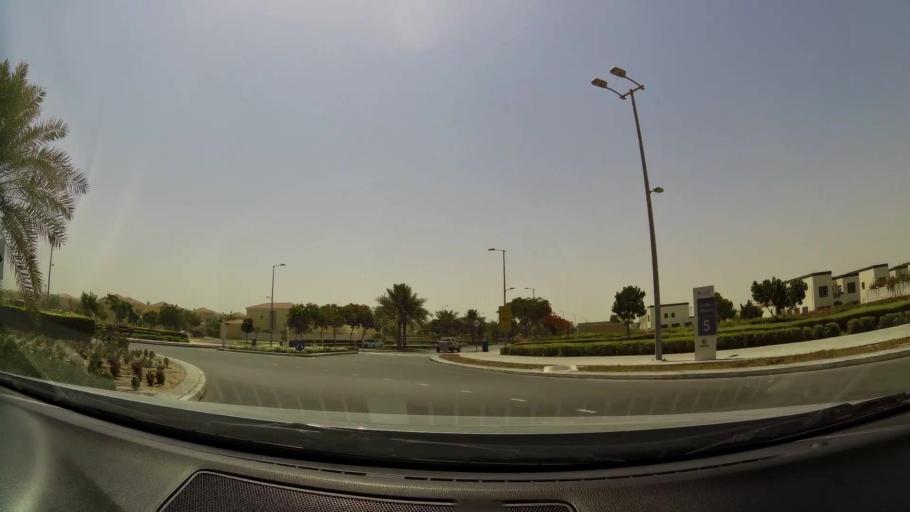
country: AE
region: Dubai
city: Dubai
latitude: 25.0498
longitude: 55.1513
